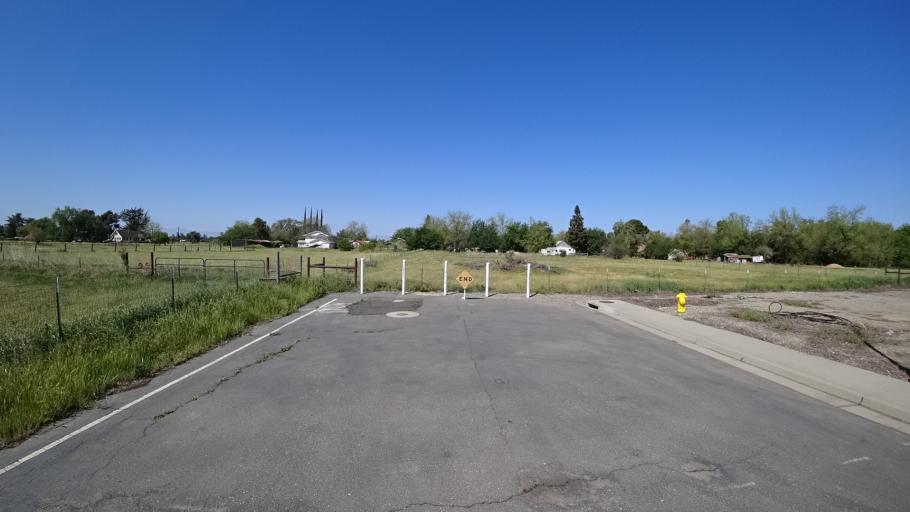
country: US
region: California
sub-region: Glenn County
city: Orland
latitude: 39.7365
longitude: -122.1851
